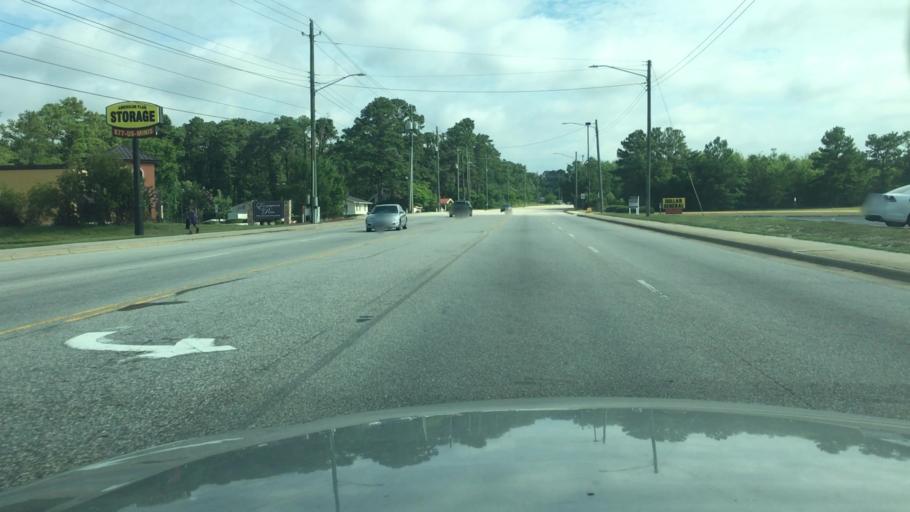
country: US
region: North Carolina
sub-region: Cumberland County
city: Hope Mills
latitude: 35.0064
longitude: -78.9670
